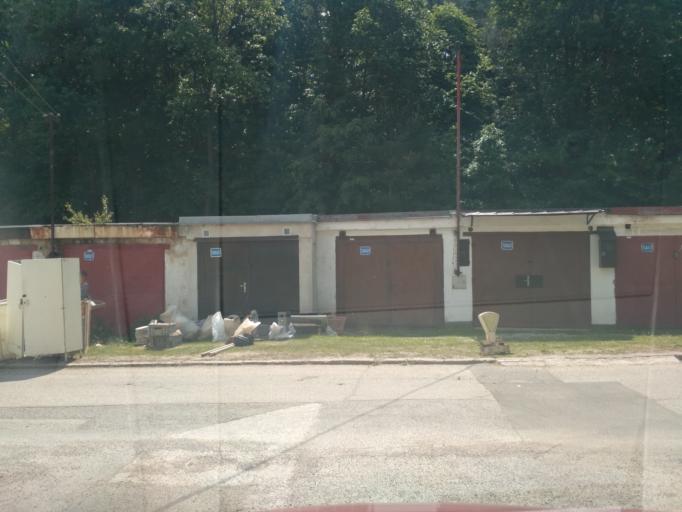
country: SK
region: Kosicky
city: Kosice
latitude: 48.7260
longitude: 21.2329
